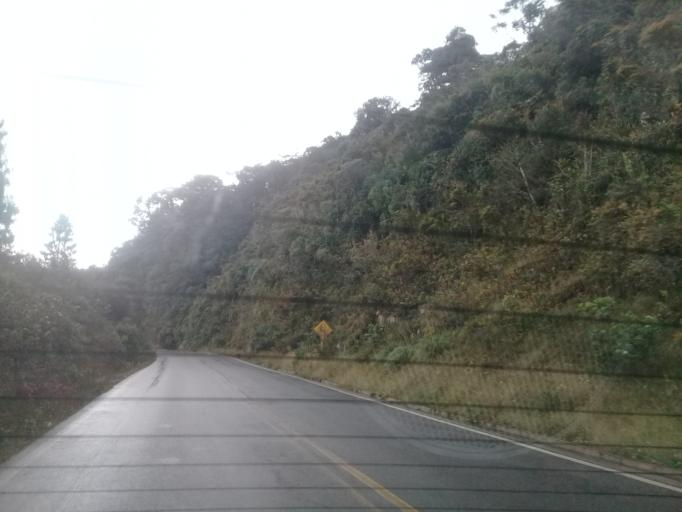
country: CO
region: Cundinamarca
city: Guatavita
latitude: 4.8578
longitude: -73.7539
